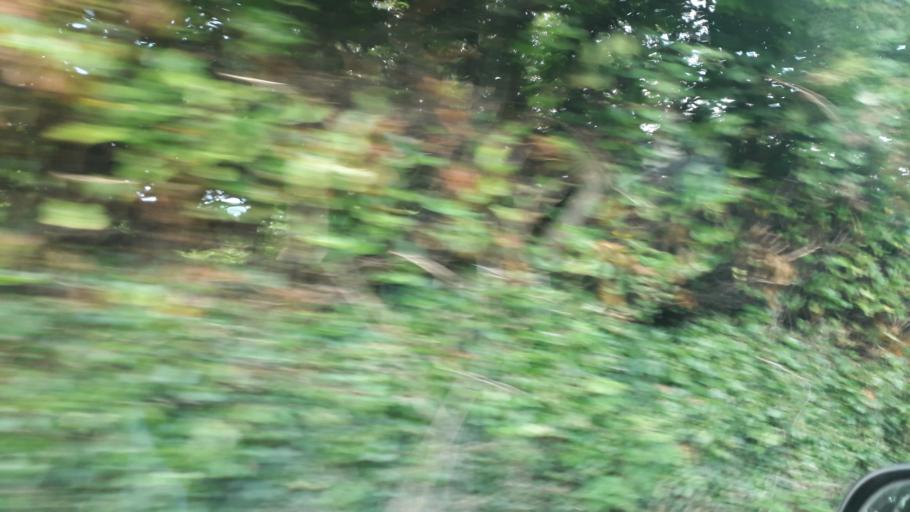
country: GB
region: Northern Ireland
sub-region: Down District
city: Warrenpoint
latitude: 54.0861
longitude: -6.2603
